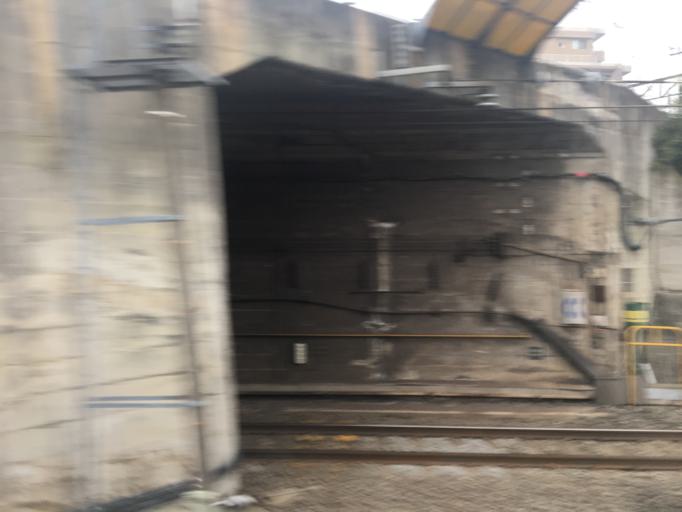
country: JP
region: Tokyo
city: Kokubunji
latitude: 35.7081
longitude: 139.4664
